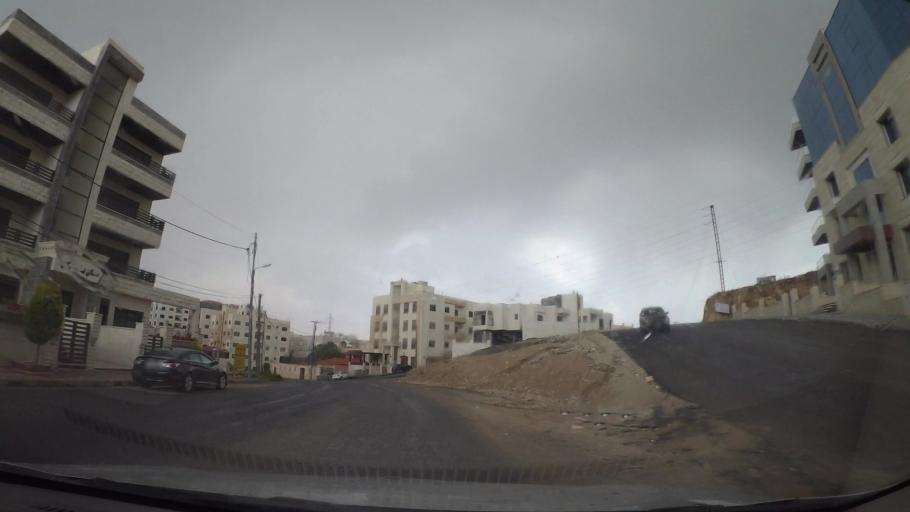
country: JO
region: Amman
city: Umm as Summaq
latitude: 31.8805
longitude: 35.8543
